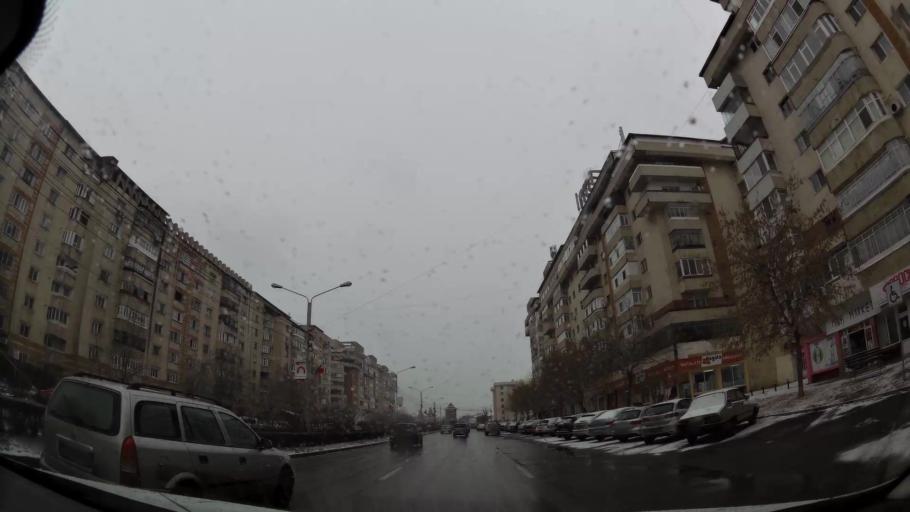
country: RO
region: Dambovita
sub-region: Municipiul Targoviste
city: Targoviste
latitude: 44.9188
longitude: 25.4790
